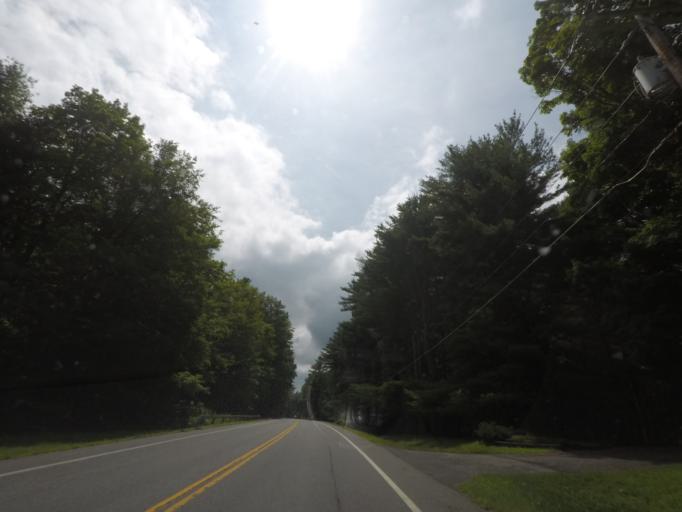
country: US
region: New York
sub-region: Saratoga County
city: Saratoga Springs
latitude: 43.0751
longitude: -73.7053
